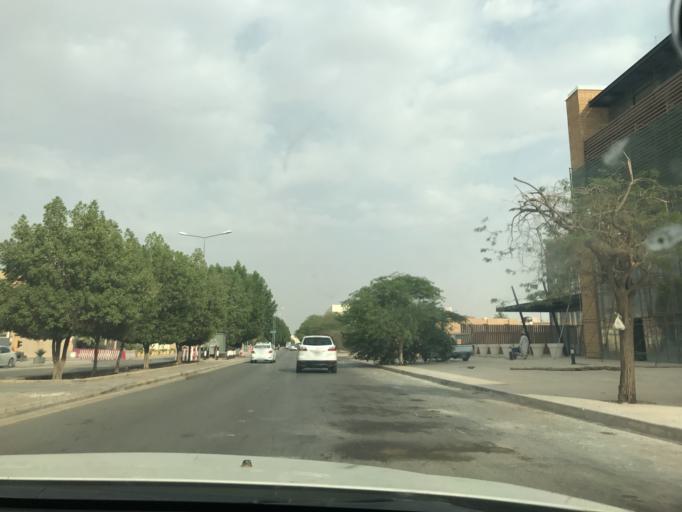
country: SA
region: Ar Riyad
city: Riyadh
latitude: 24.7070
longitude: 46.7078
